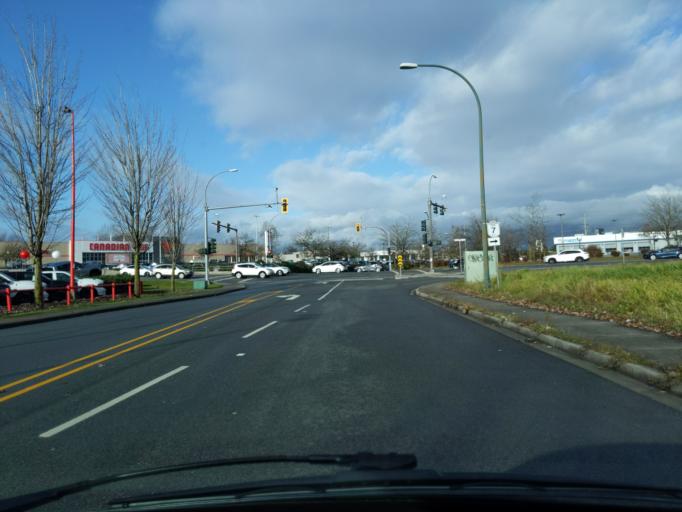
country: CA
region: British Columbia
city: Pitt Meadows
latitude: 49.2200
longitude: -122.6659
